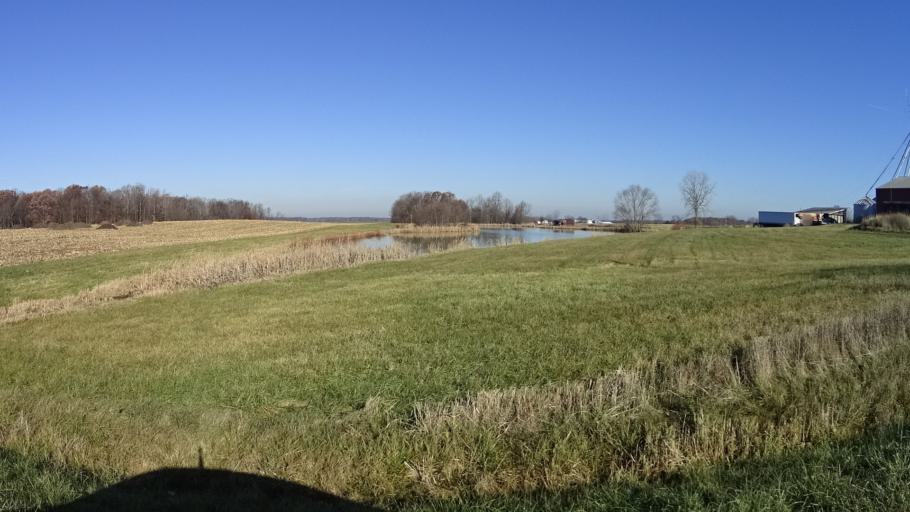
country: US
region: Ohio
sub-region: Lorain County
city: Wellington
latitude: 41.0705
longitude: -82.2240
